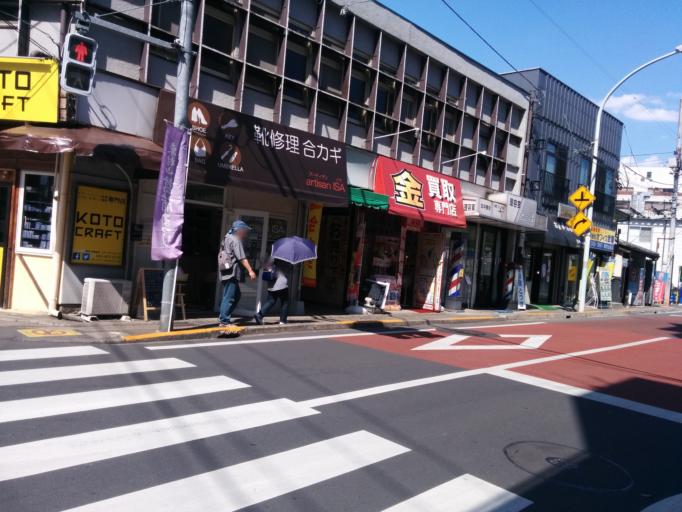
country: JP
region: Tokyo
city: Higashimurayama-shi
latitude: 35.7613
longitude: 139.4648
